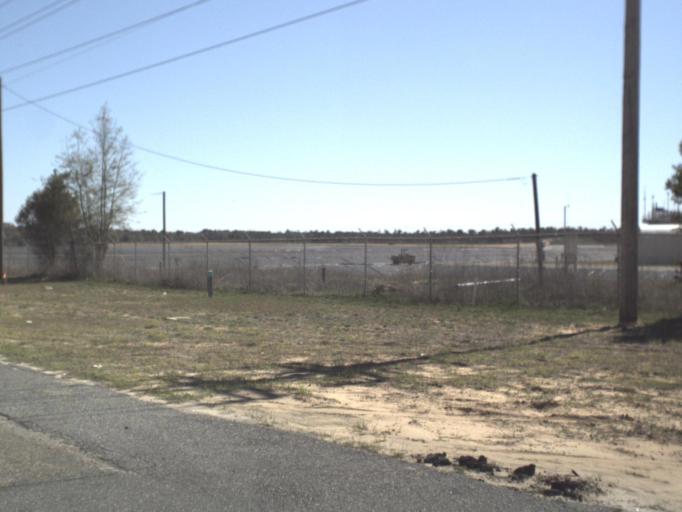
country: US
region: Florida
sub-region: Leon County
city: Tallahassee
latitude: 30.3921
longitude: -84.3196
